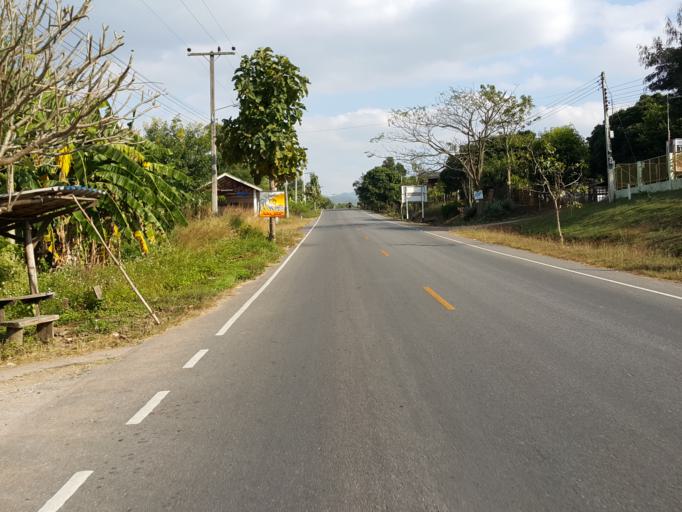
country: TH
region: Lamphun
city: Ban Hong
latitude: 18.2624
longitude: 98.9400
